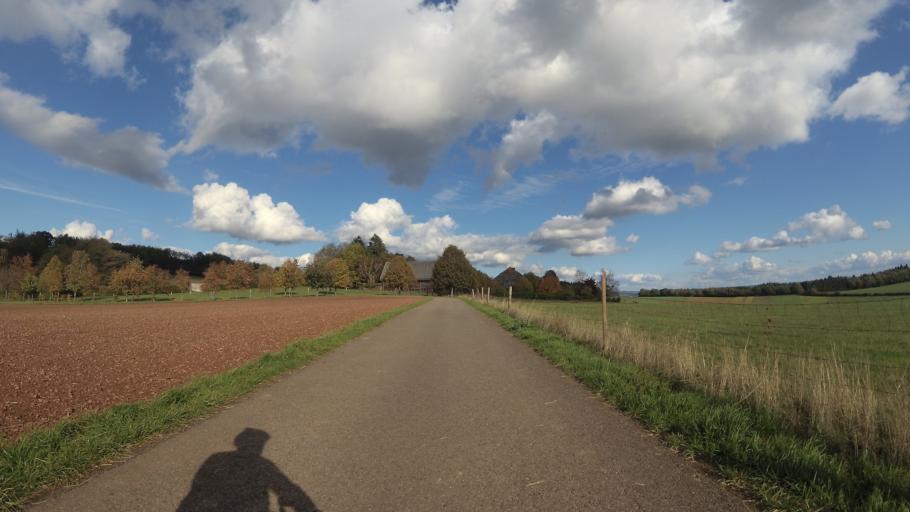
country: DE
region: Saarland
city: Marpingen
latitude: 49.4501
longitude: 7.0809
